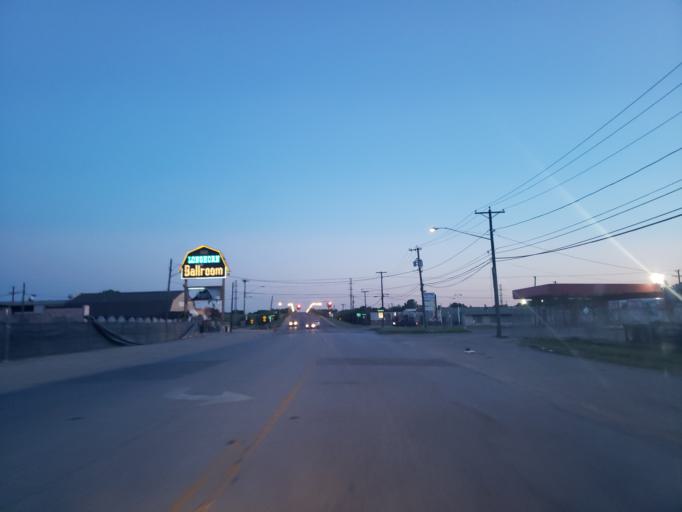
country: US
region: Texas
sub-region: Dallas County
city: Dallas
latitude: 32.7609
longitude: -96.7935
